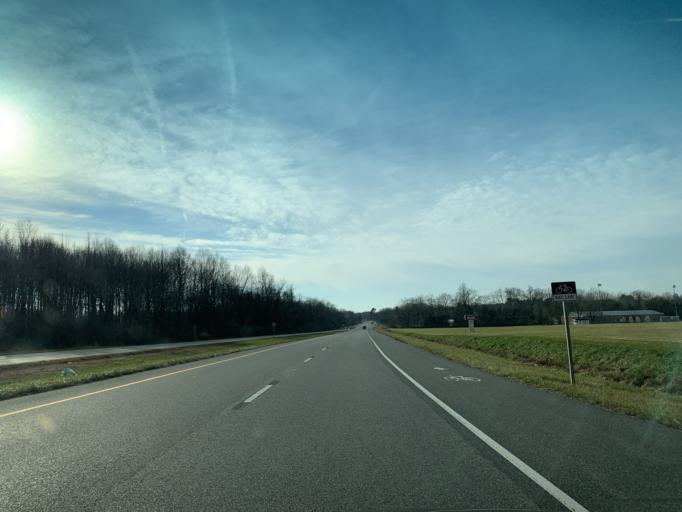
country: US
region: Maryland
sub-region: Cecil County
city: Elkton
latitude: 39.6234
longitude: -75.8203
